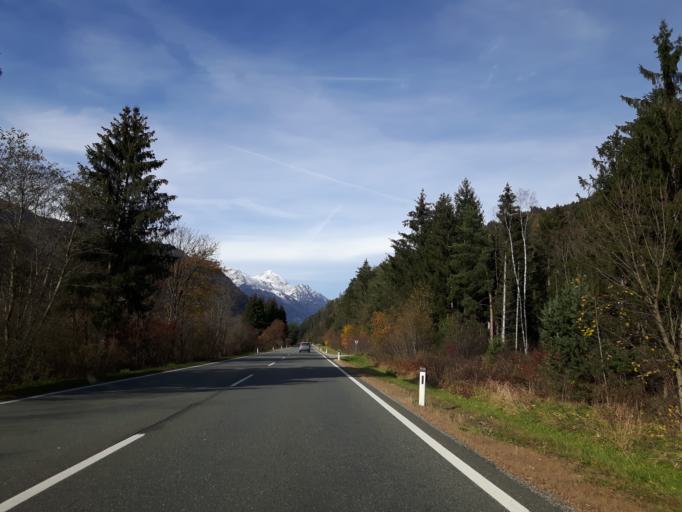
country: AT
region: Tyrol
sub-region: Politischer Bezirk Lienz
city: Schlaiten
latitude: 46.8750
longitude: 12.6764
